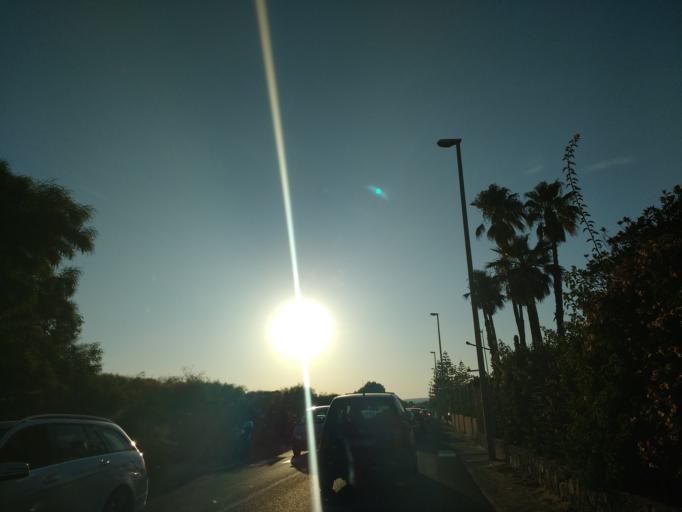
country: IT
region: Sicily
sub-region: Ragusa
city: Ispica
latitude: 36.7243
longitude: 14.9128
